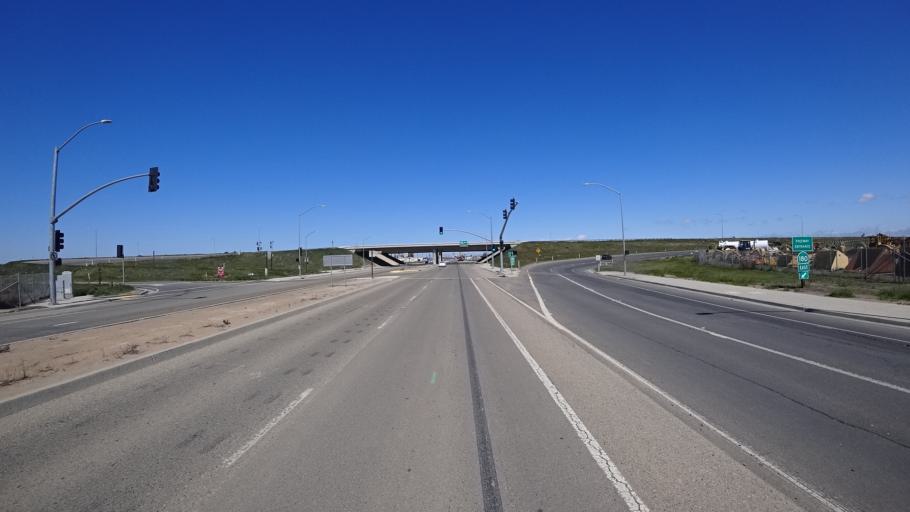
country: US
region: California
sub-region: Fresno County
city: West Park
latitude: 36.7369
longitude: -119.8443
